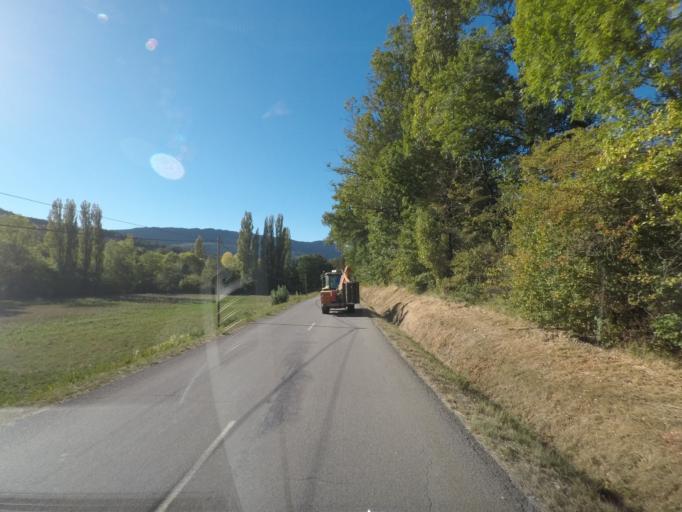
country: FR
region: Rhone-Alpes
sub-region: Departement de la Drome
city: Buis-les-Baronnies
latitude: 44.4794
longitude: 5.4017
